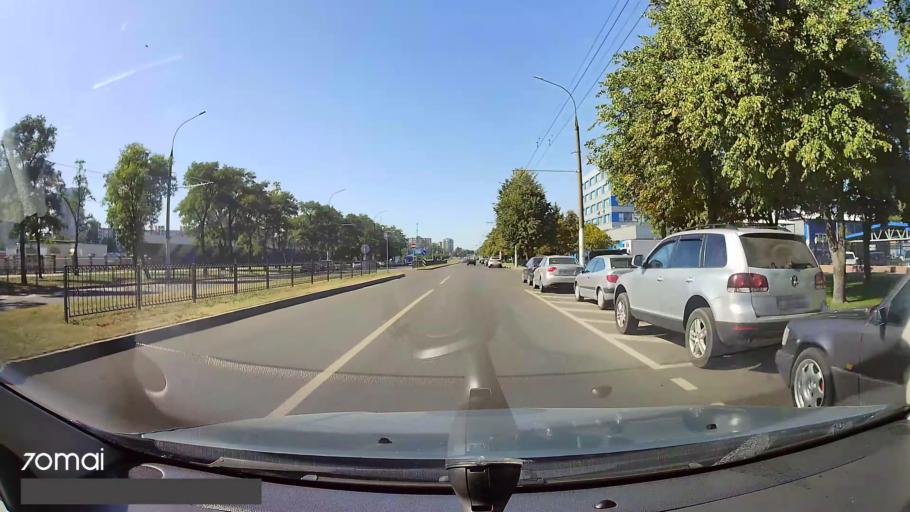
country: BY
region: Brest
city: Brest
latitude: 52.1127
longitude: 23.7665
